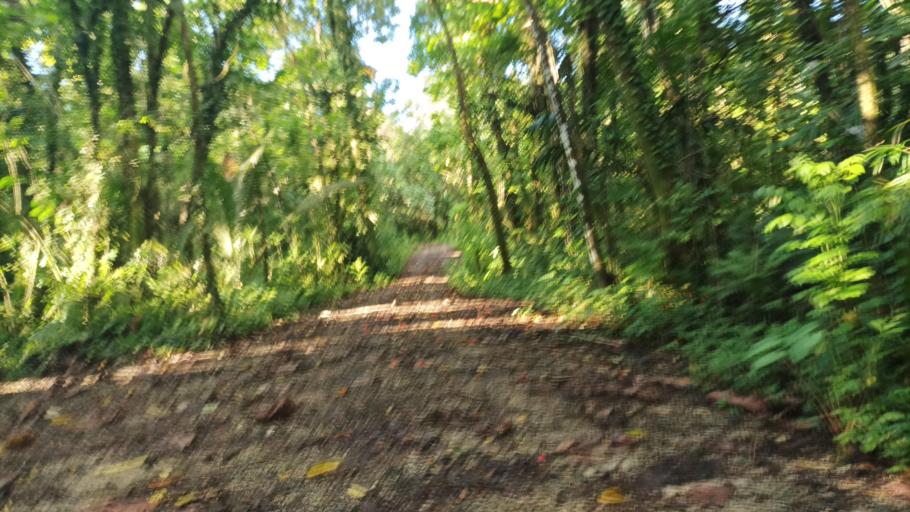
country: FM
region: Pohnpei
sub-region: Kolonia Municipality
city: Kolonia Town
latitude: 6.9670
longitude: 158.1866
